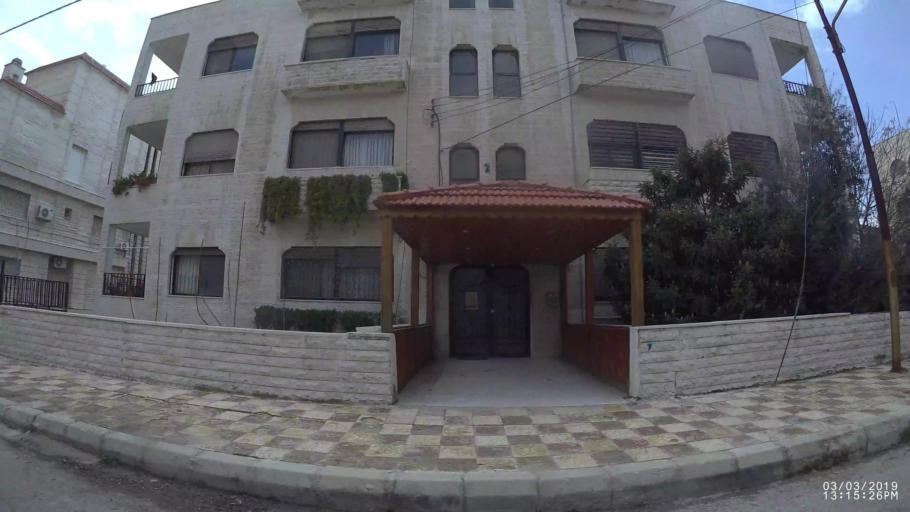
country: JO
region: Amman
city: Amman
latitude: 31.9815
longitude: 35.8969
